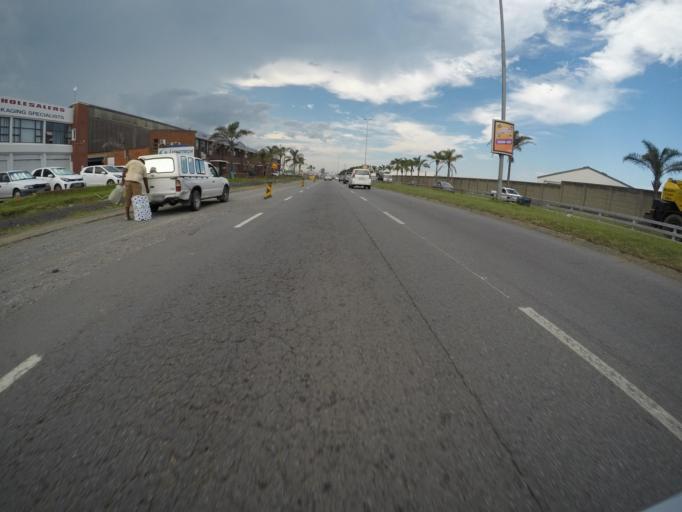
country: ZA
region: Eastern Cape
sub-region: Buffalo City Metropolitan Municipality
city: East London
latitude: -33.0292
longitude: 27.8875
